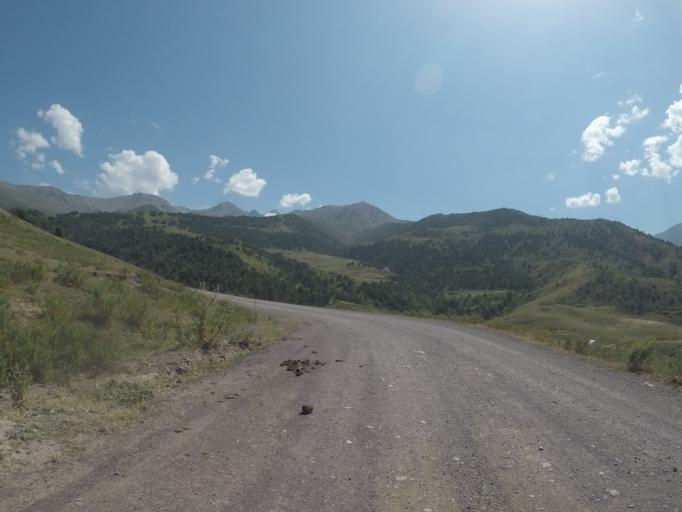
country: KG
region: Chuy
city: Bishkek
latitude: 42.6476
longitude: 74.5169
